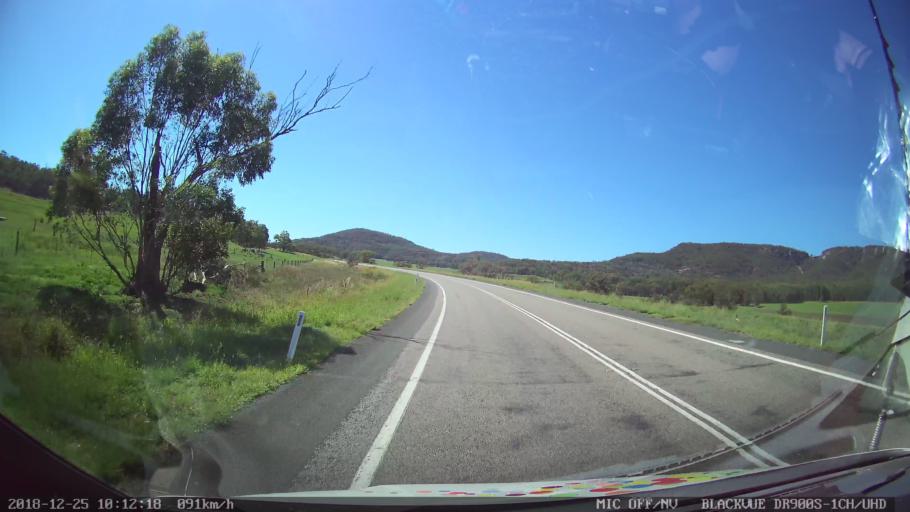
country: AU
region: New South Wales
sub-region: Muswellbrook
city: Denman
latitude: -32.3272
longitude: 150.5299
